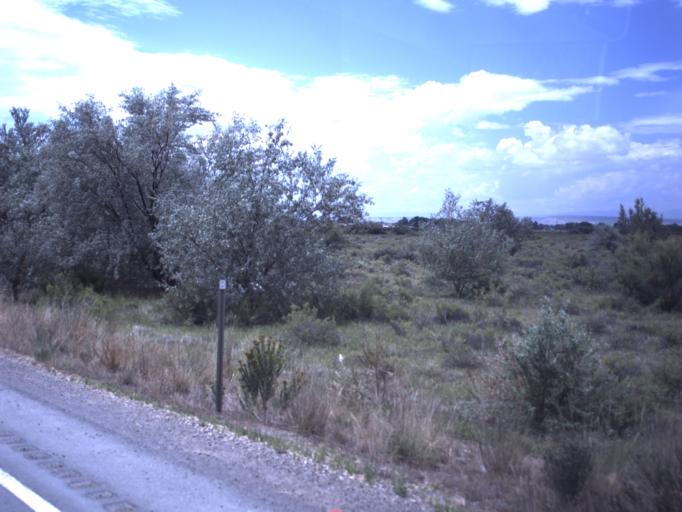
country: US
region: Utah
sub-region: Duchesne County
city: Roosevelt
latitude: 40.1877
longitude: -110.0906
